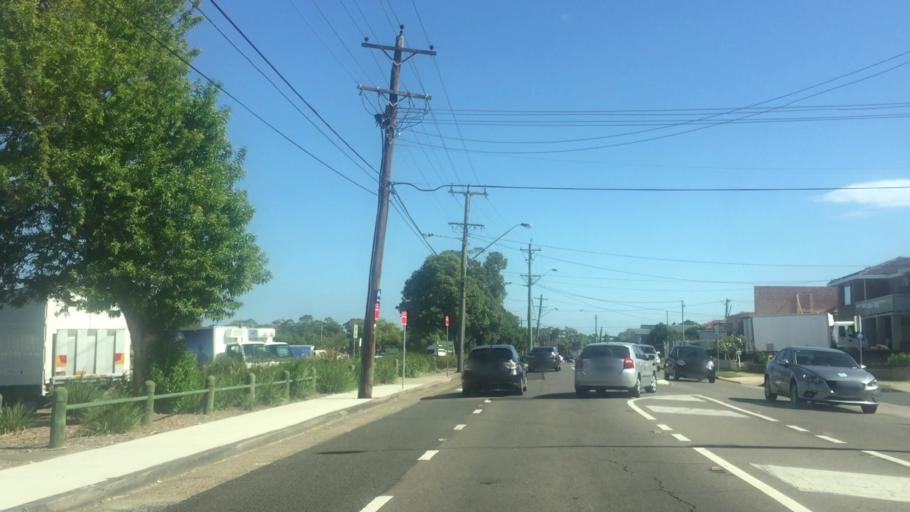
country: AU
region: New South Wales
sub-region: Holroyd
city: Merrylands
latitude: -33.8311
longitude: 150.9777
